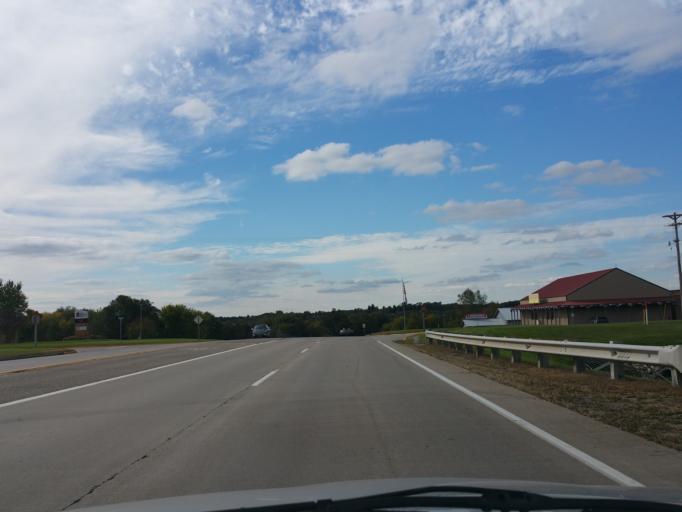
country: US
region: Wisconsin
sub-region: Pierce County
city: Prescott
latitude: 44.7610
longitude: -92.7959
